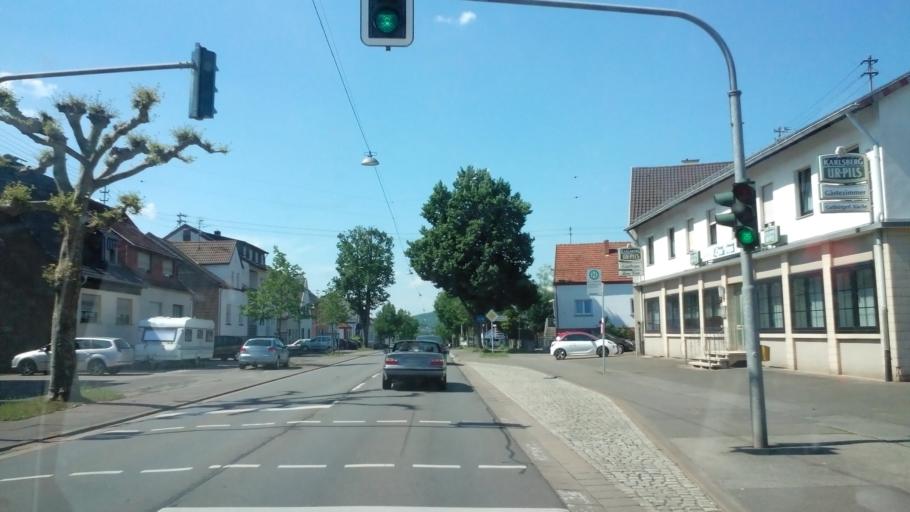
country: DE
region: Saarland
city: Saarwellingen
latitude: 49.3635
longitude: 6.7986
